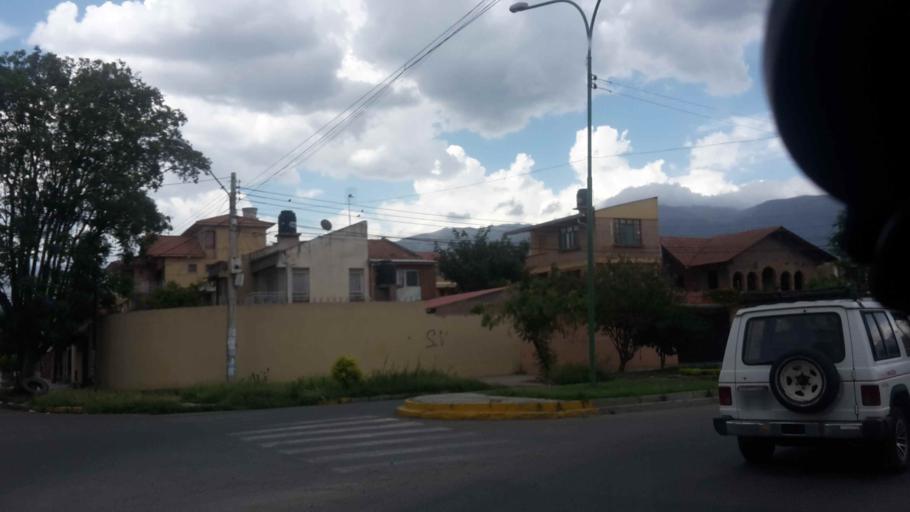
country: BO
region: Cochabamba
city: Cochabamba
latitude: -17.3998
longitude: -66.1723
